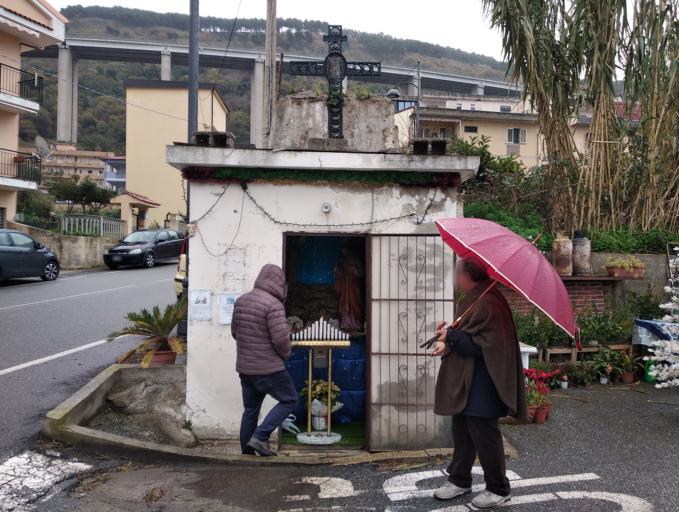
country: IT
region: Calabria
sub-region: Provincia di Vibo-Valentia
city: Maierato
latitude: 38.7339
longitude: 16.1665
